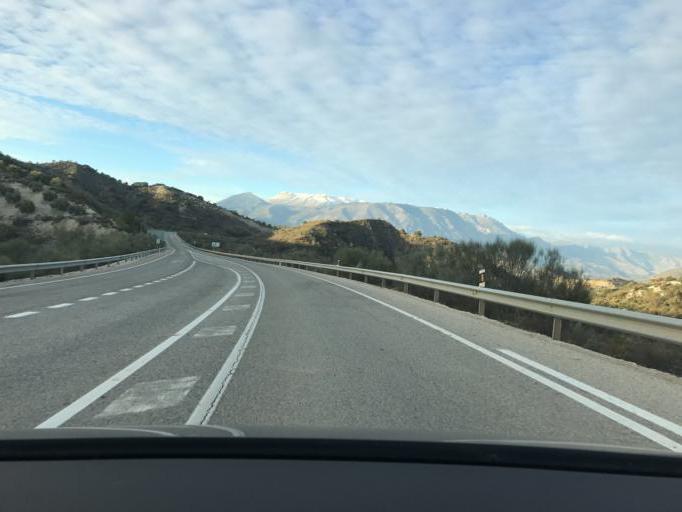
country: ES
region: Andalusia
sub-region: Provincia de Jaen
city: Guadahortuna
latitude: 37.6163
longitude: -3.3950
